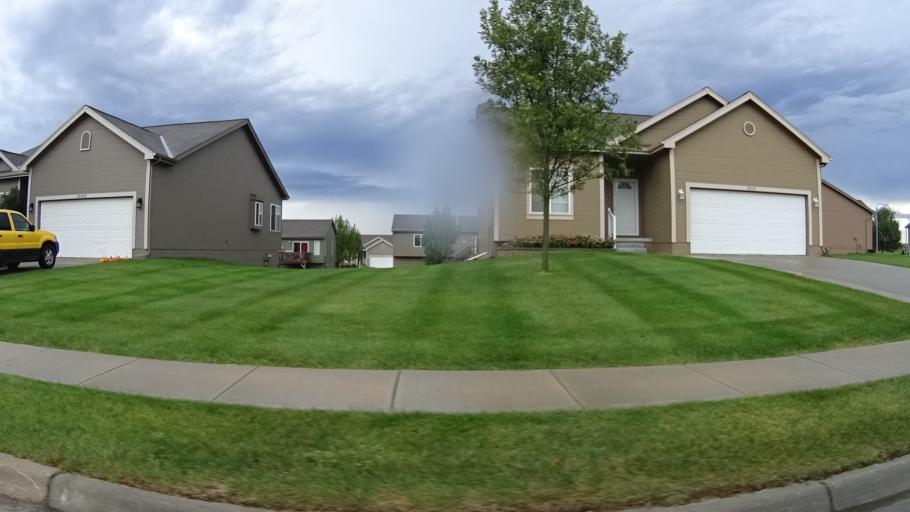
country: US
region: Nebraska
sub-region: Sarpy County
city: Offutt Air Force Base
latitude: 41.1557
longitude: -95.9484
